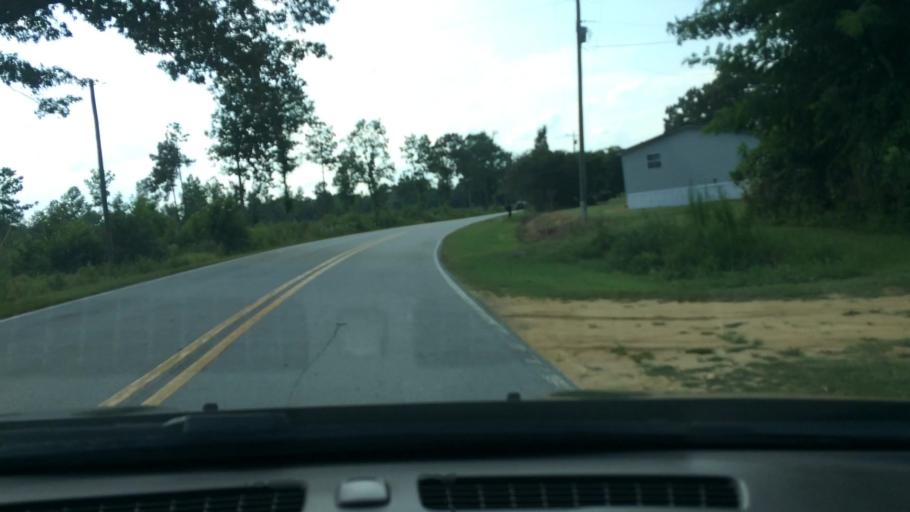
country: US
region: North Carolina
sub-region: Beaufort County
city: River Road
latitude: 35.4315
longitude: -76.9804
